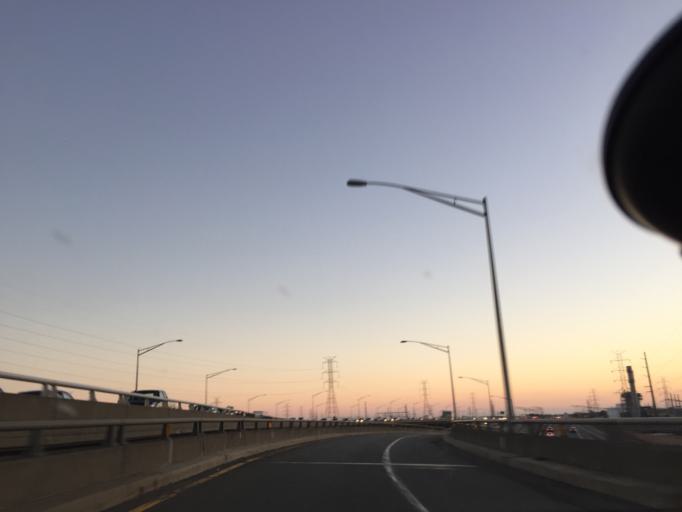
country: US
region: New Jersey
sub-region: Union County
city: Elizabeth
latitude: 40.6377
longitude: -74.2087
